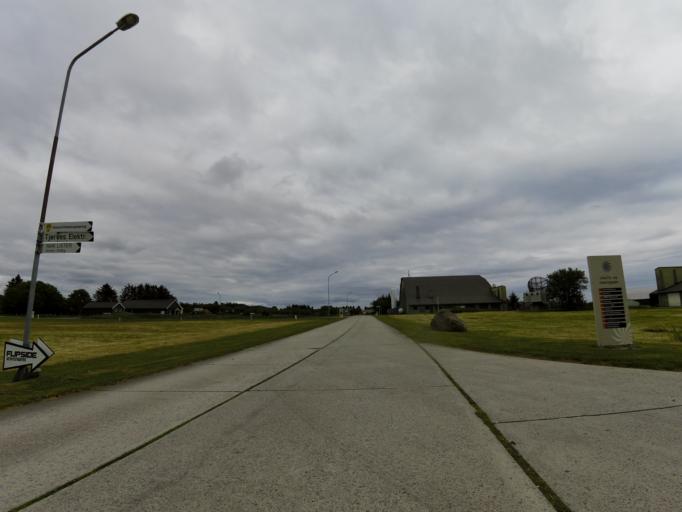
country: NO
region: Vest-Agder
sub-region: Farsund
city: Vestbygd
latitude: 58.1143
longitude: 6.6148
